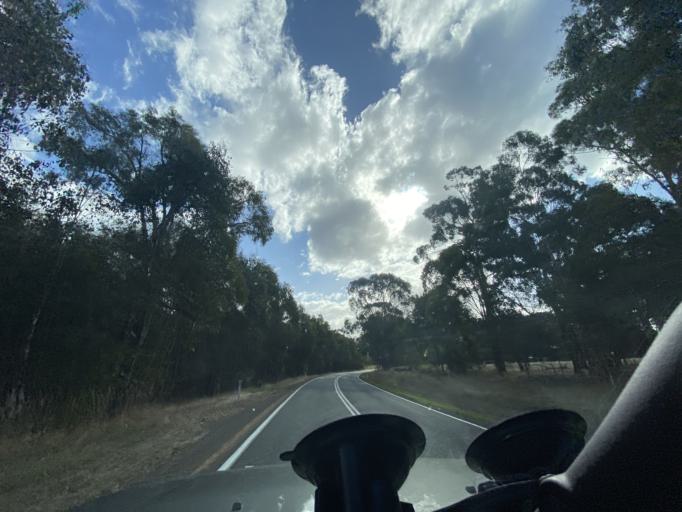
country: AU
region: Victoria
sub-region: Murrindindi
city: Kinglake West
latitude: -37.3221
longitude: 145.3017
